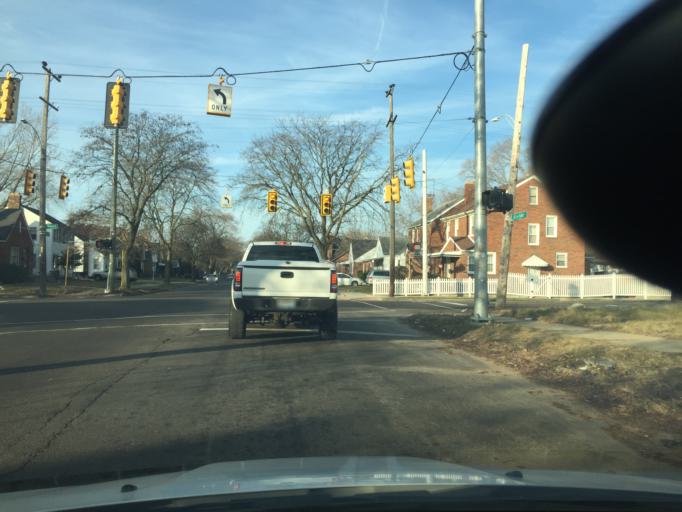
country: US
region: Michigan
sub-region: Macomb County
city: Eastpointe
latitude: 42.4427
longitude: -82.9654
